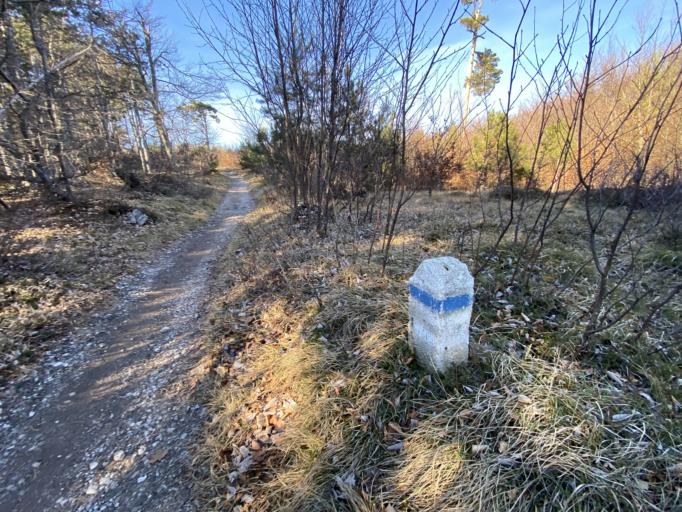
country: AT
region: Lower Austria
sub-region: Politischer Bezirk Baden
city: Heiligenkreuz
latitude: 48.0028
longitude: 16.1476
